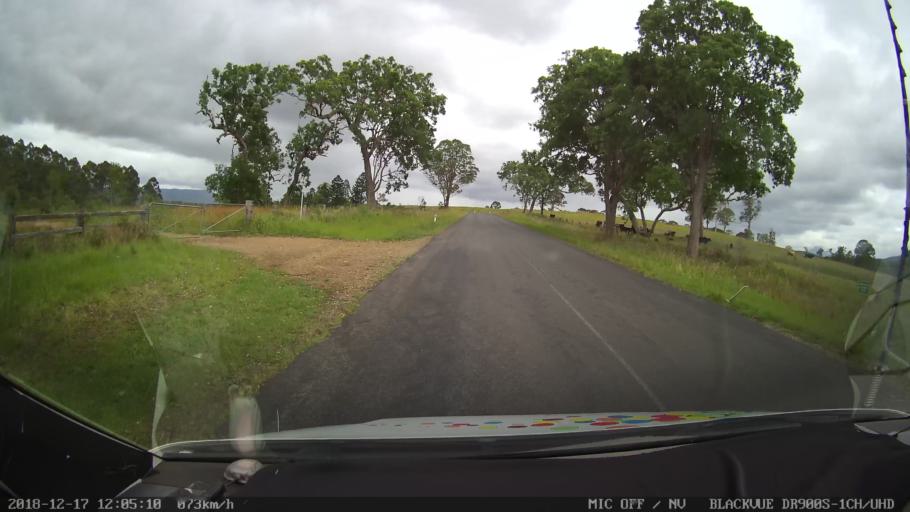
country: AU
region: New South Wales
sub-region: Kyogle
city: Kyogle
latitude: -28.4951
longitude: 152.5674
